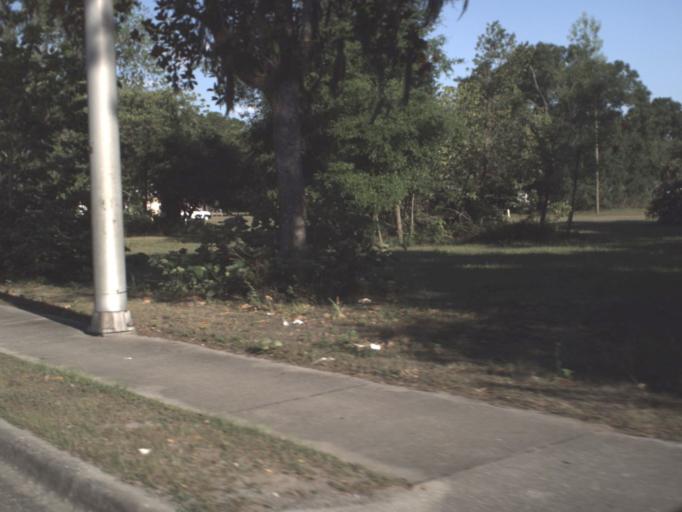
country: US
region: Florida
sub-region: Marion County
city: Ocala
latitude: 29.1860
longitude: -82.1560
